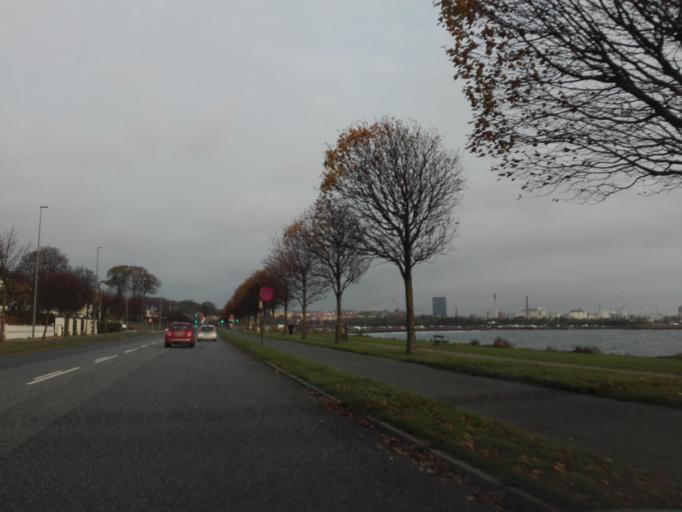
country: DK
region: Central Jutland
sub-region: Arhus Kommune
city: Arhus
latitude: 56.1335
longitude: 10.2106
